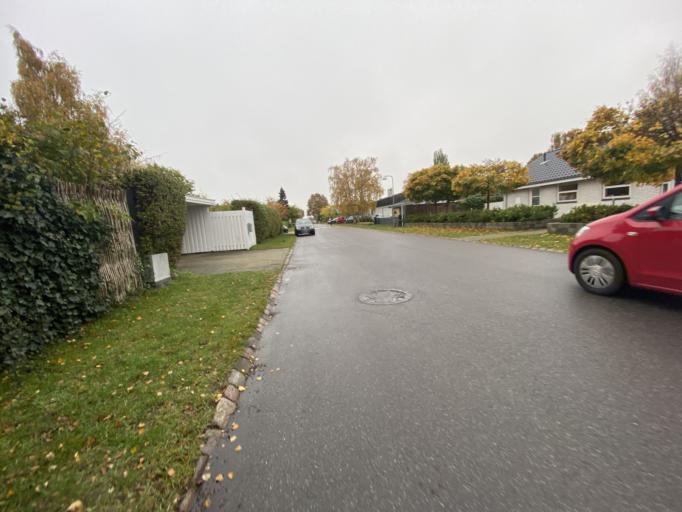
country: DK
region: Capital Region
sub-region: Dragor Kommune
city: Dragor
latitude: 55.5684
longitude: 12.6097
